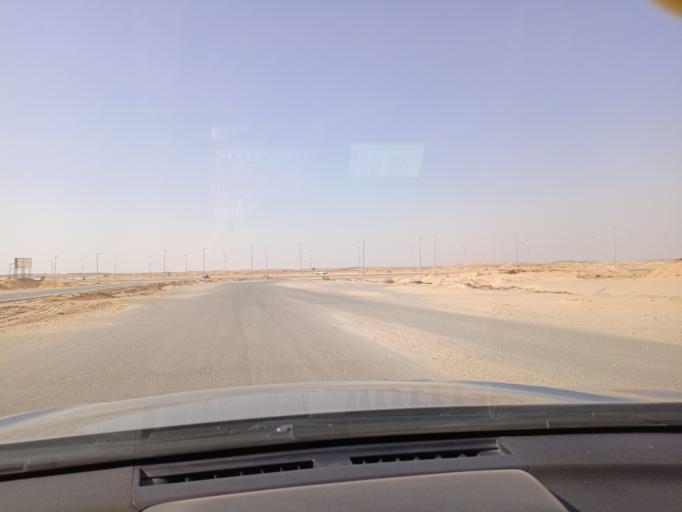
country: EG
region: Muhafazat al Qalyubiyah
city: Al Khankah
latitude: 30.0425
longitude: 31.7137
